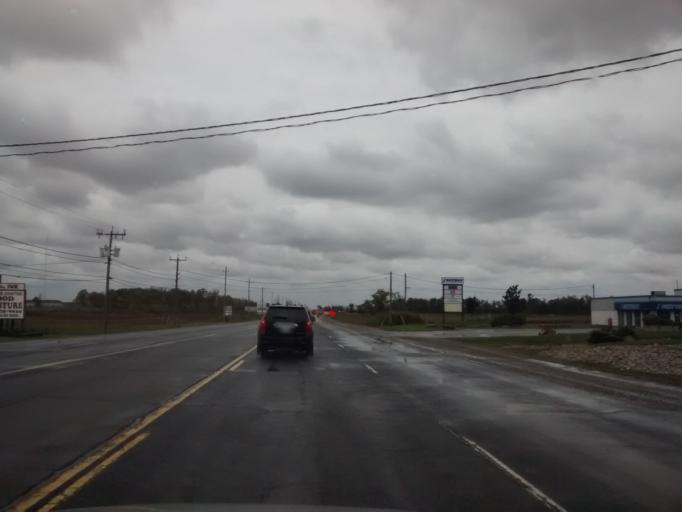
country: CA
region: Ontario
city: Hamilton
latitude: 43.1826
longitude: -79.7725
